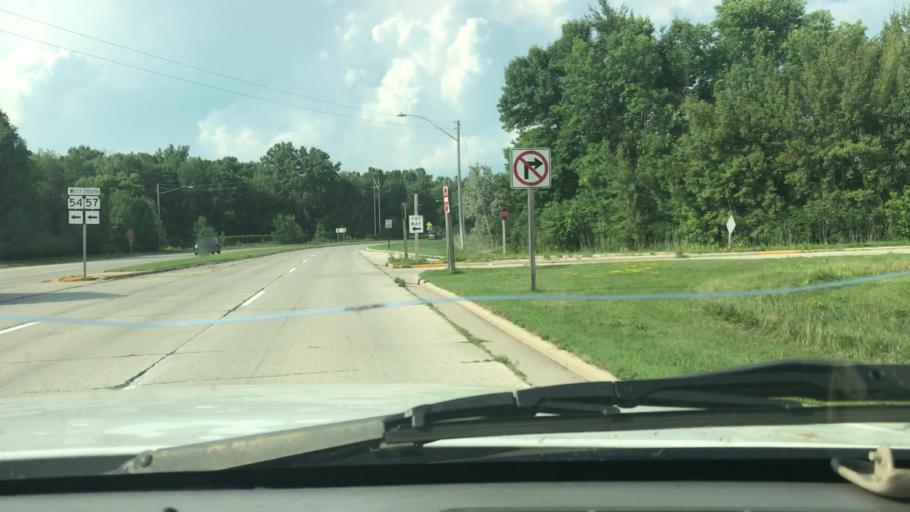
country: US
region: Wisconsin
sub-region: Brown County
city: Green Bay
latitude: 44.5258
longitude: -87.9407
